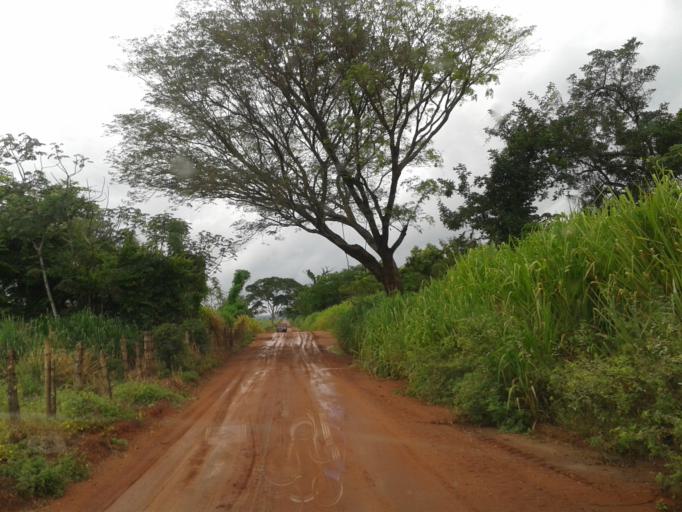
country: BR
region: Minas Gerais
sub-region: Santa Vitoria
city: Santa Vitoria
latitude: -18.7051
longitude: -49.9594
